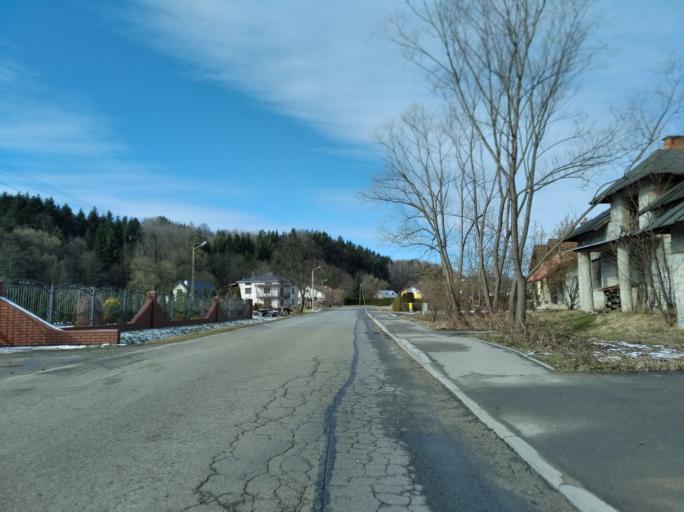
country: PL
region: Subcarpathian Voivodeship
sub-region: Powiat brzozowski
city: Jasienica Rosielna
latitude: 49.7470
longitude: 21.9211
